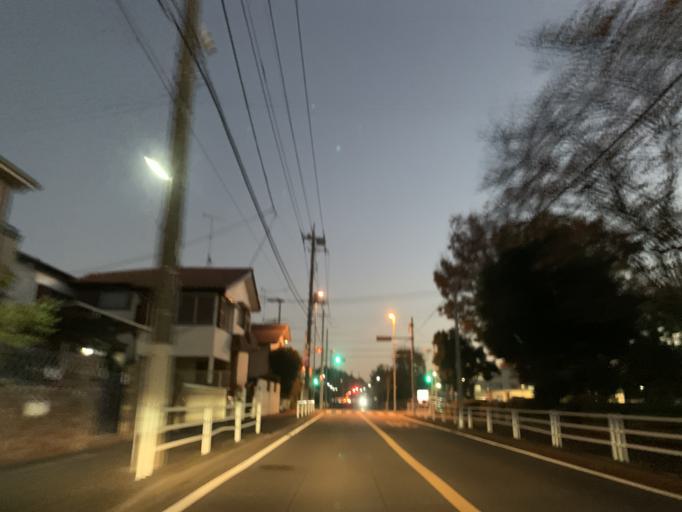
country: JP
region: Chiba
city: Nagareyama
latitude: 35.8945
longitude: 139.9095
